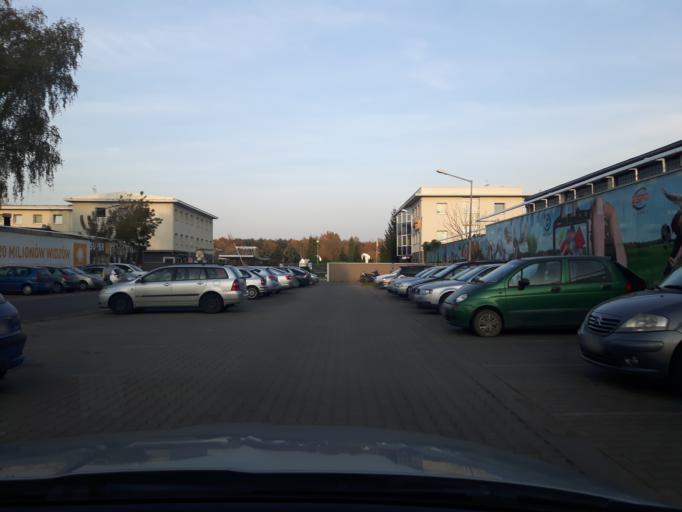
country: PL
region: Masovian Voivodeship
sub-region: Warszawa
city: Praga Poludnie
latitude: 52.2623
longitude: 21.0965
